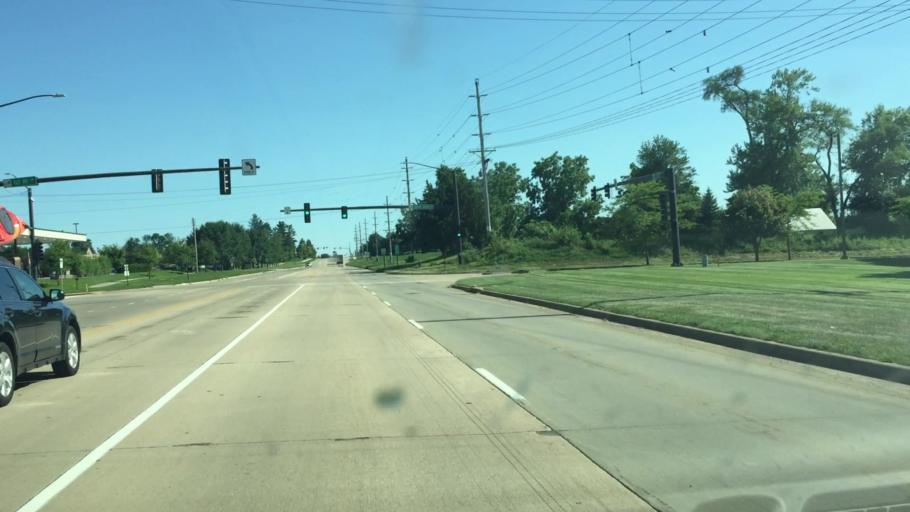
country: US
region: Iowa
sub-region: Linn County
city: Ely
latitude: 41.9237
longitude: -91.6374
